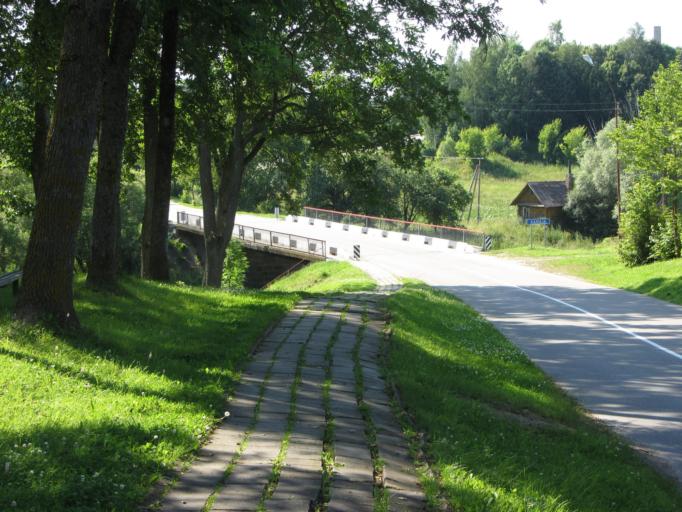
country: BY
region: Vitebsk
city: Vidzy
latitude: 55.1559
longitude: 26.5903
